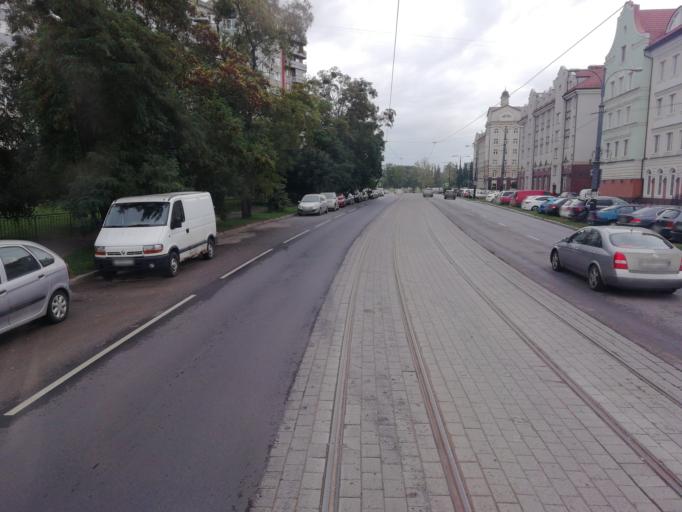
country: RU
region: Kaliningrad
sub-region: Gorod Kaliningrad
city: Kaliningrad
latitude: 54.7038
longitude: 20.5161
